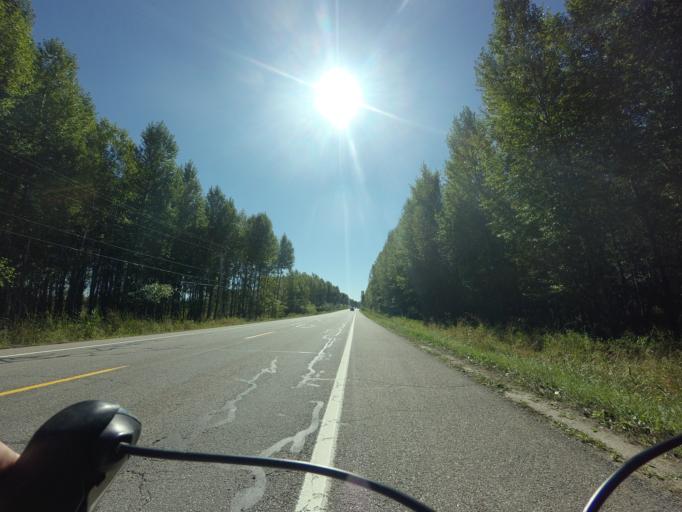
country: CA
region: Ontario
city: Clarence-Rockland
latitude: 45.5381
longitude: -75.4144
